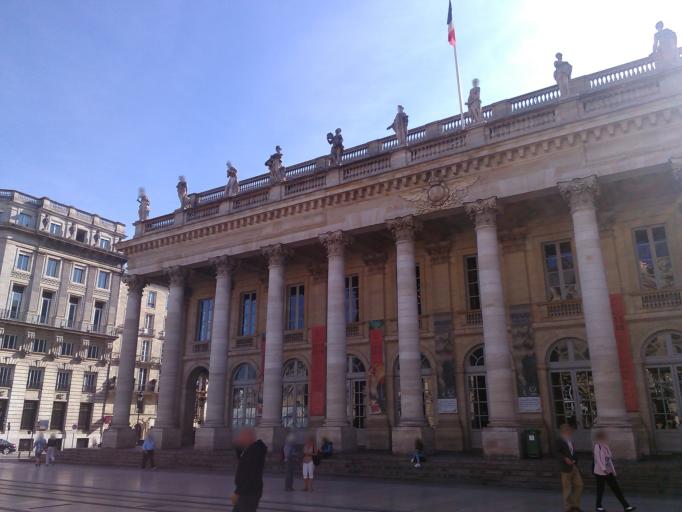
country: FR
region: Aquitaine
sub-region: Departement de la Gironde
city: Bordeaux
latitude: 44.8425
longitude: -0.5746
